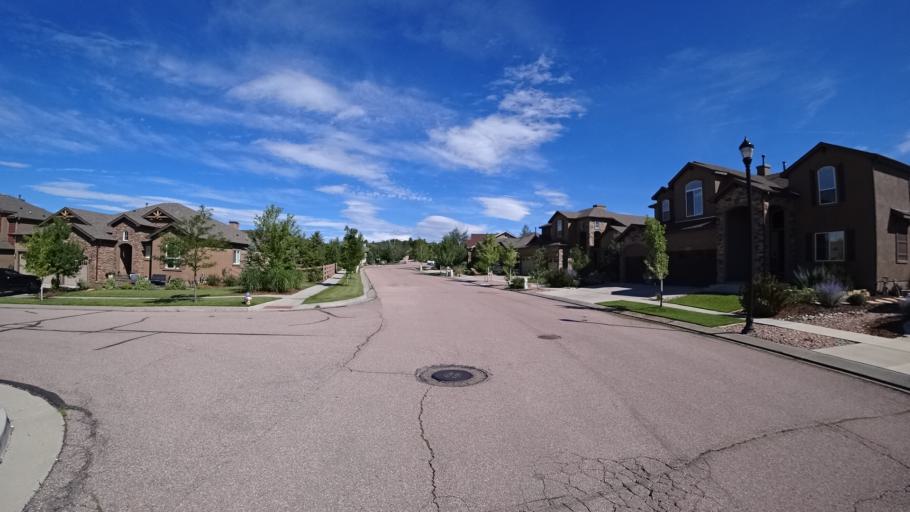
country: US
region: Colorado
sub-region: El Paso County
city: Gleneagle
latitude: 39.0252
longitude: -104.8047
